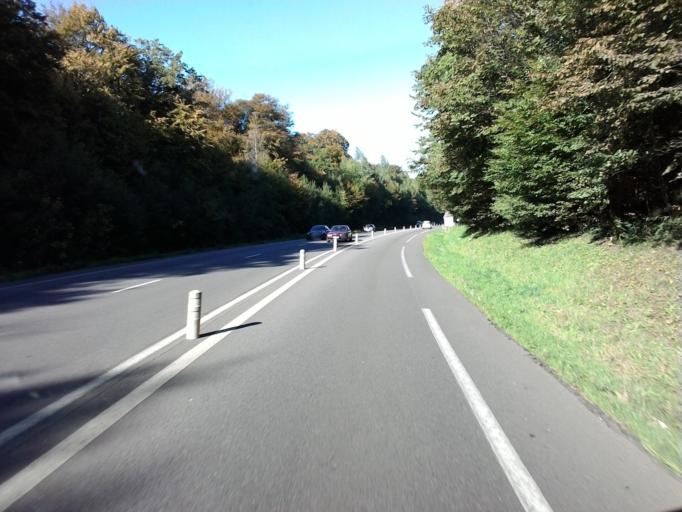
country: FR
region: Lorraine
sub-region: Departement de Meurthe-et-Moselle
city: Longwy
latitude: 49.5387
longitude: 5.7564
